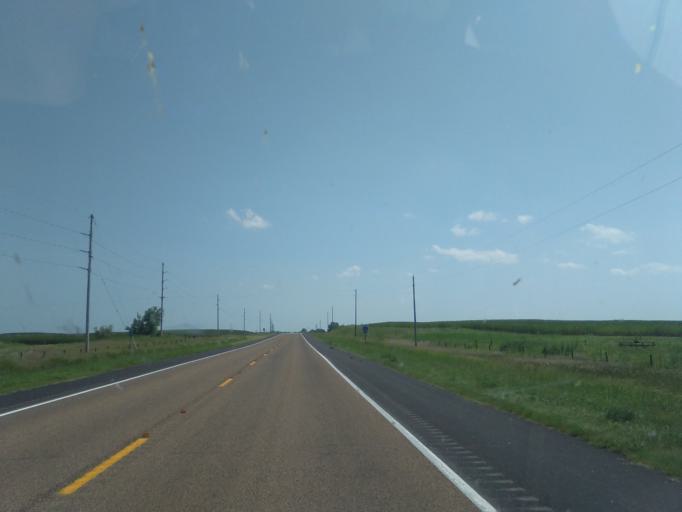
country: US
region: Nebraska
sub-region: Phelps County
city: Holdrege
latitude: 40.6500
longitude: -99.3807
